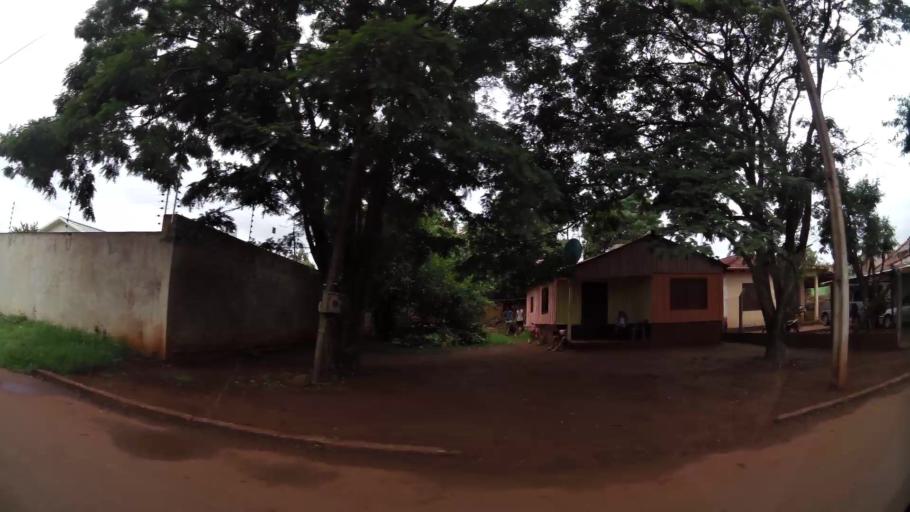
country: PY
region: Alto Parana
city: Ciudad del Este
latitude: -25.4798
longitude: -54.7671
